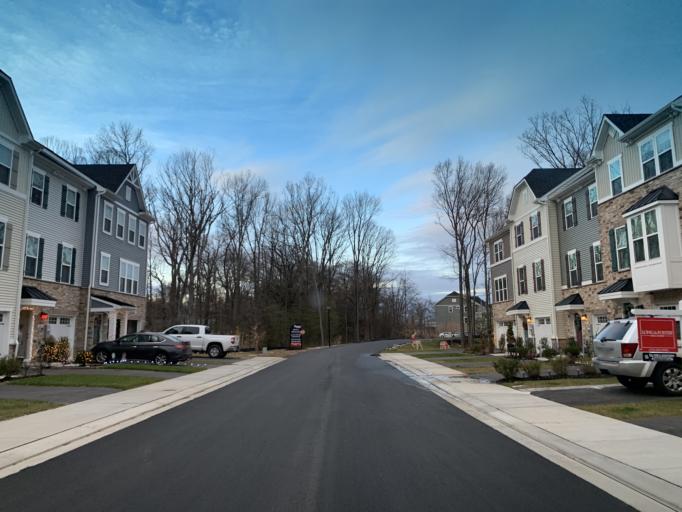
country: US
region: Maryland
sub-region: Baltimore County
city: Edgemere
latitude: 39.2338
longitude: -76.4361
